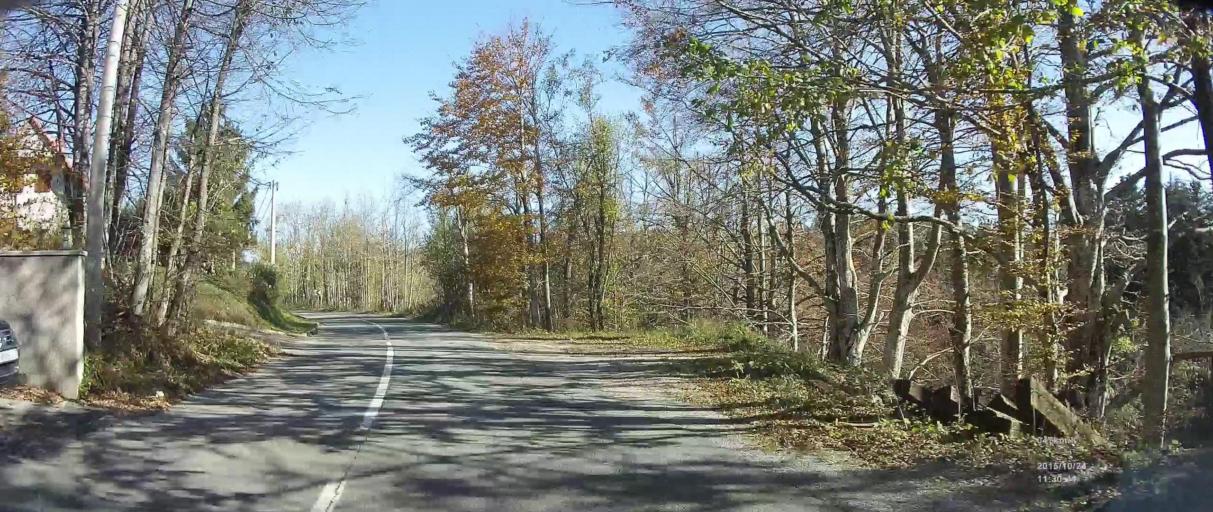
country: HR
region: Primorsko-Goranska
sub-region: Grad Delnice
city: Delnice
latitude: 45.3808
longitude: 14.6840
